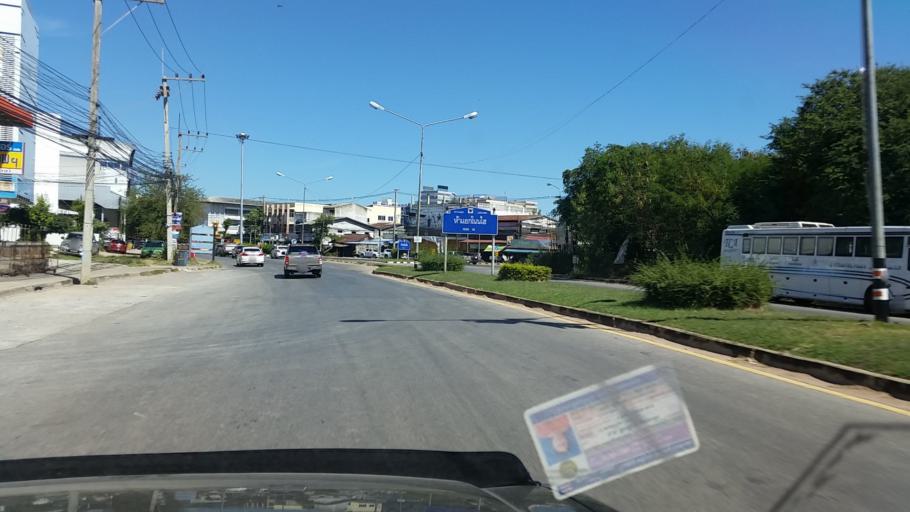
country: TH
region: Chaiyaphum
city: Chaiyaphum
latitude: 15.8013
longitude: 102.0303
